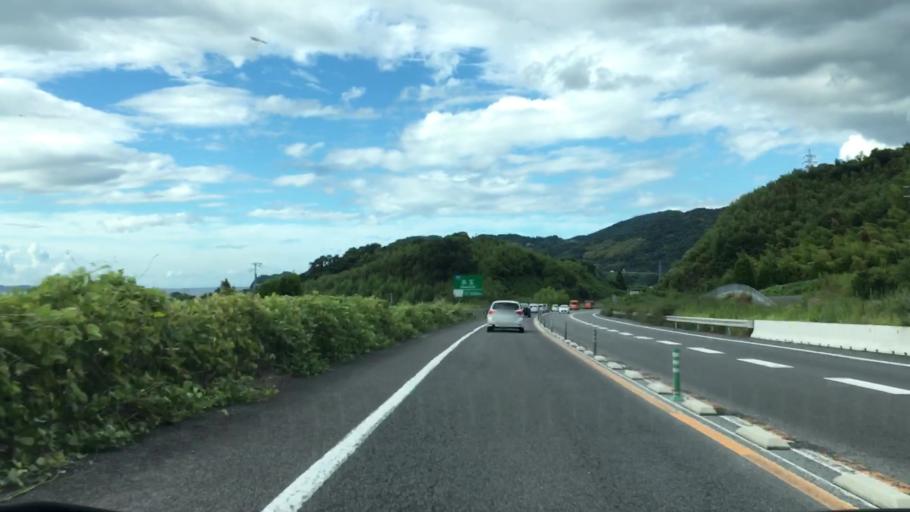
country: JP
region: Saga Prefecture
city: Karatsu
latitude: 33.4364
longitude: 130.0479
